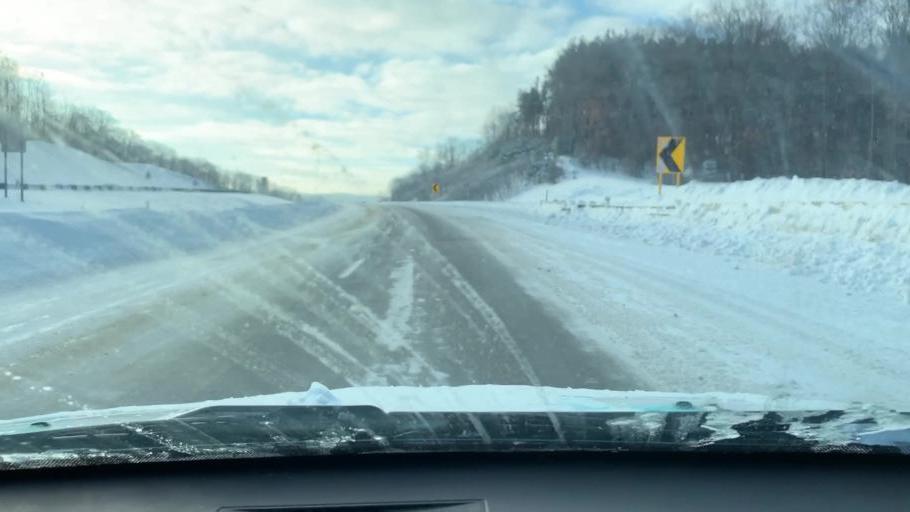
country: US
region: Michigan
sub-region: Wexford County
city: Cadillac
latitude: 44.2992
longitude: -85.3923
